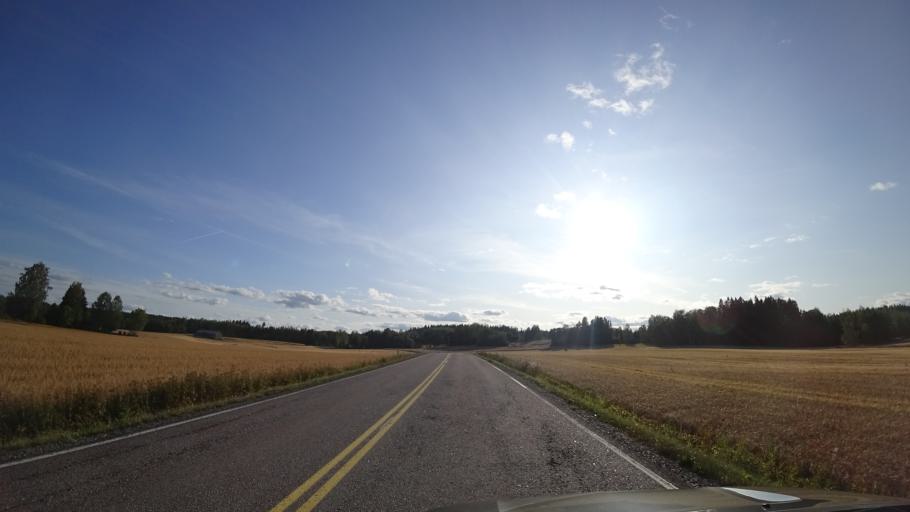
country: FI
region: Paijanne Tavastia
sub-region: Lahti
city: Asikkala
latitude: 61.1828
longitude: 25.3844
